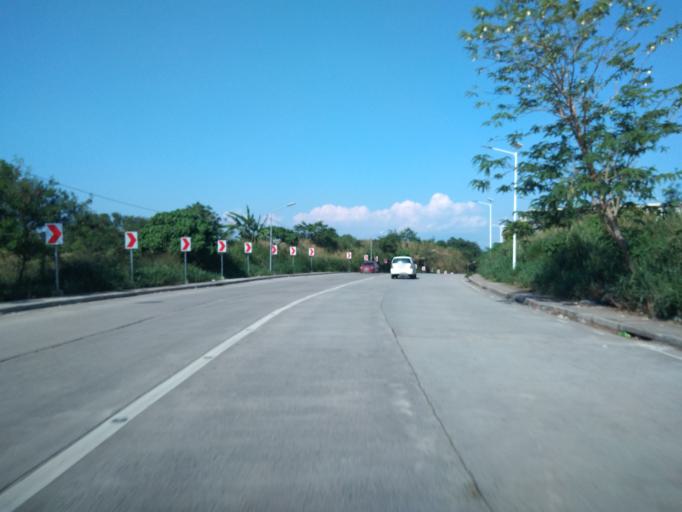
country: PH
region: Calabarzon
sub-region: Province of Laguna
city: Prinza
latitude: 14.1840
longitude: 121.1606
